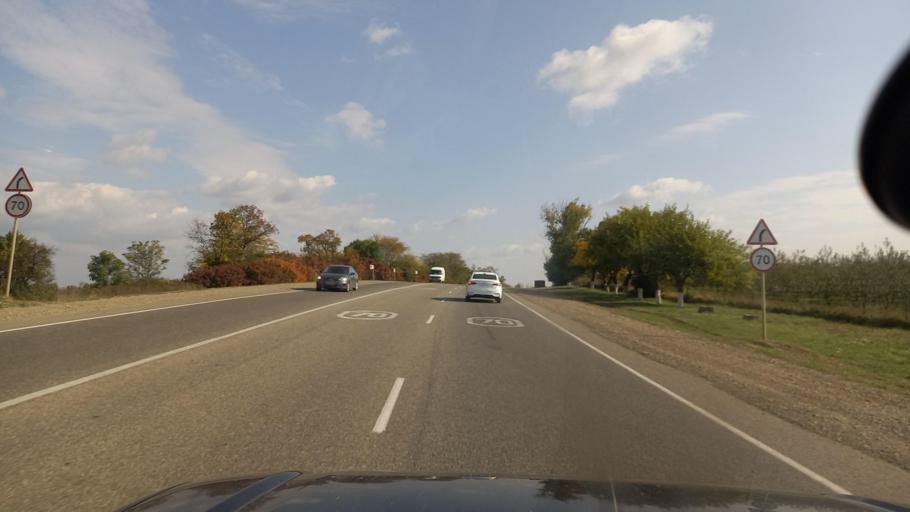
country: RU
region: Krasnodarskiy
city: Akhtyrskiy
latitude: 44.8542
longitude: 38.3246
